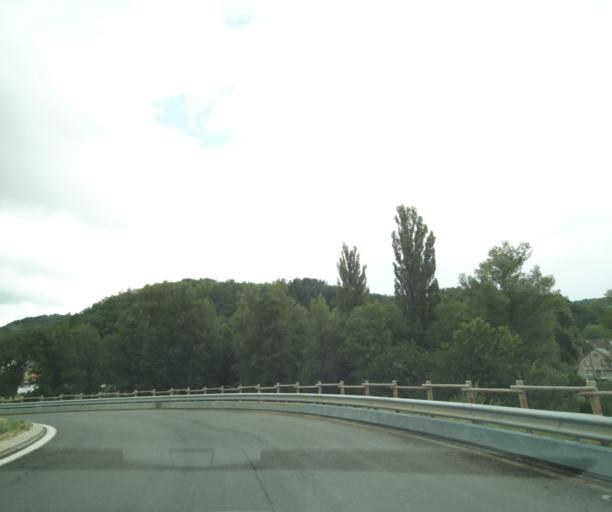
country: FR
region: Languedoc-Roussillon
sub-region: Departement de la Lozere
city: La Canourgue
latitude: 44.4386
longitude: 3.1976
